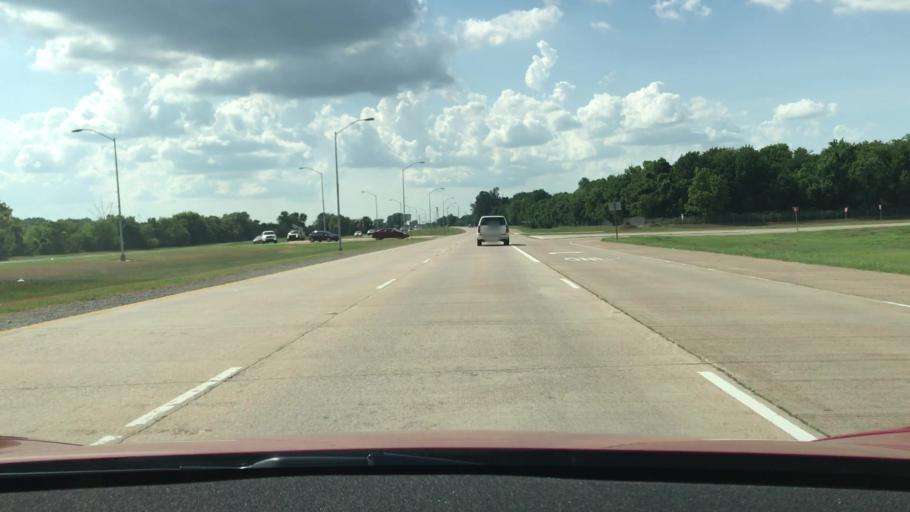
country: US
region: Louisiana
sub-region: Bossier Parish
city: Bossier City
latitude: 32.4952
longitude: -93.6972
